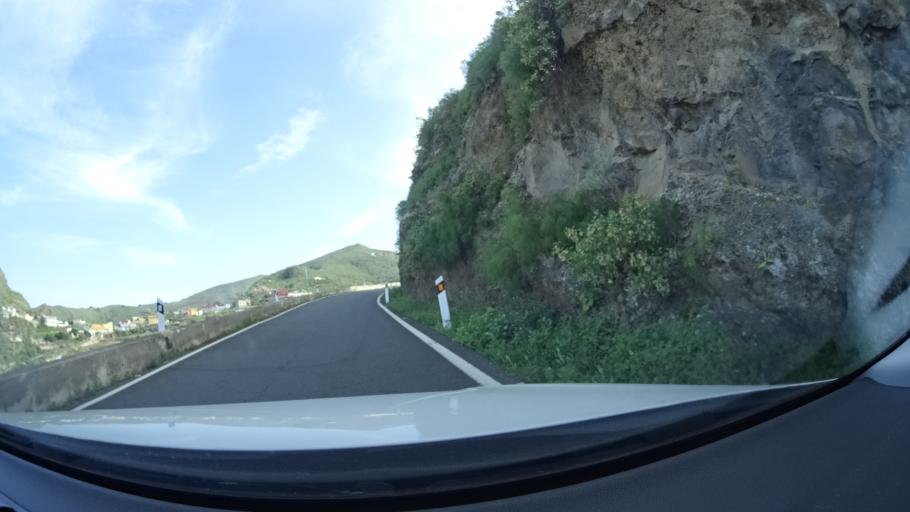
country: ES
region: Canary Islands
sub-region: Provincia de Las Palmas
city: Guia
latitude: 28.1160
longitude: -15.6420
